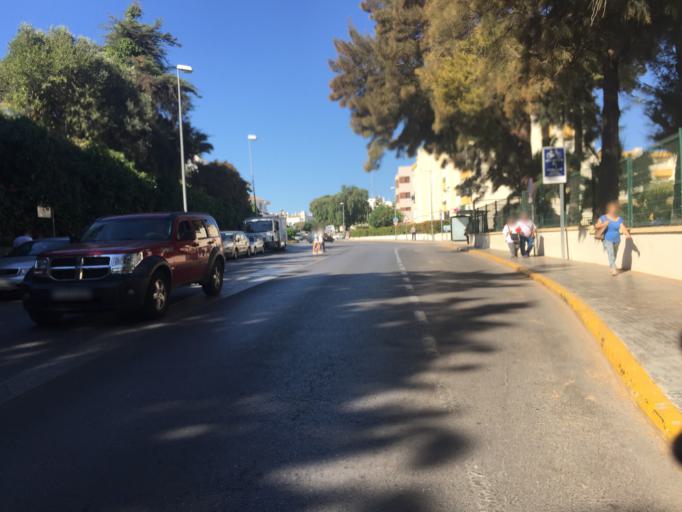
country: ES
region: Andalusia
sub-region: Provincia de Cadiz
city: Chiclana de la Frontera
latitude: 36.4187
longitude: -6.1542
